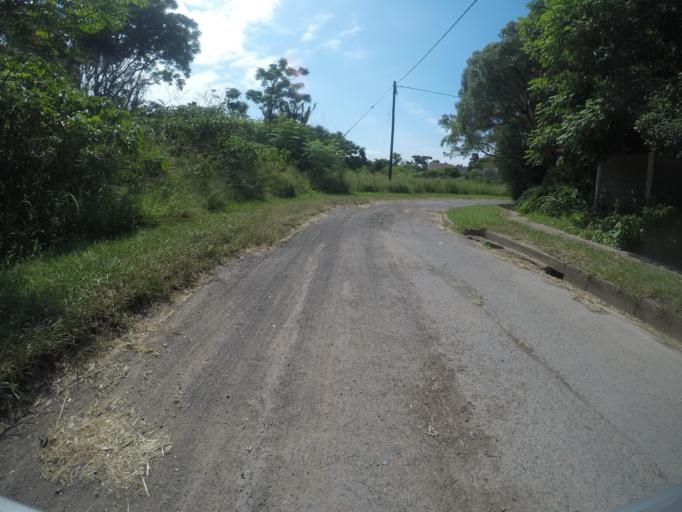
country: ZA
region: Eastern Cape
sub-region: Buffalo City Metropolitan Municipality
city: East London
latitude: -32.9822
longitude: 27.8727
